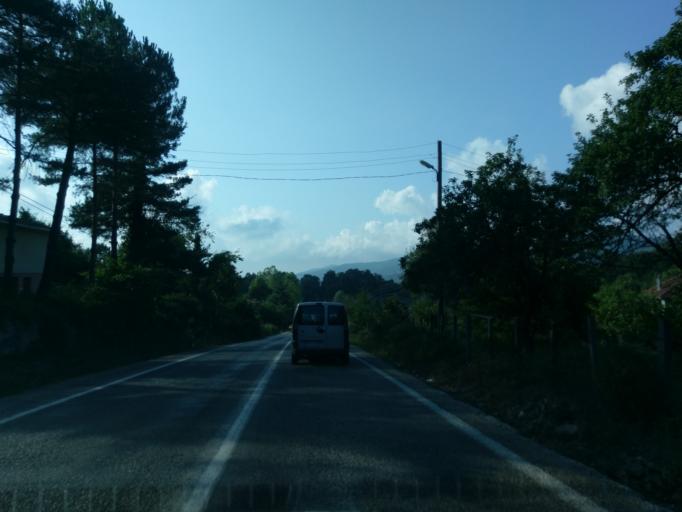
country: TR
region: Sinop
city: Ayancik
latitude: 41.8791
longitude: 34.5074
